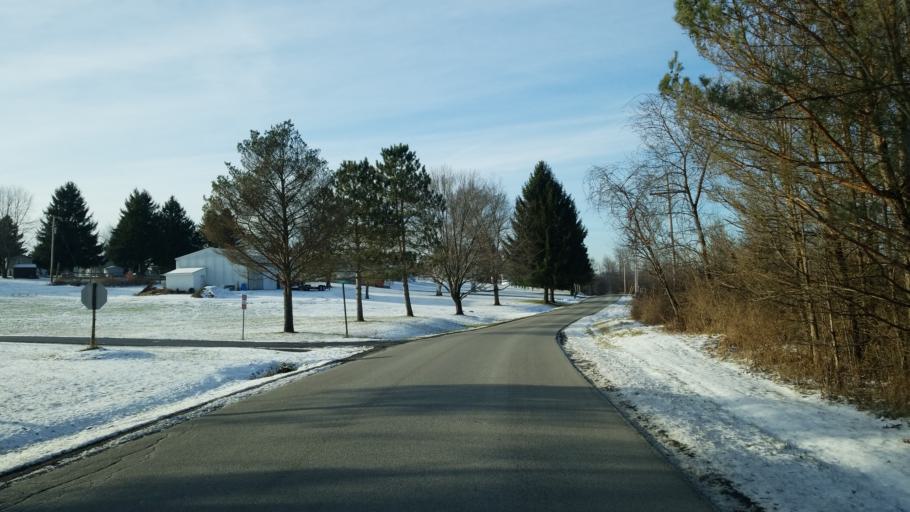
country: US
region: Pennsylvania
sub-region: Clearfield County
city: DuBois
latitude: 41.1099
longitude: -78.6984
